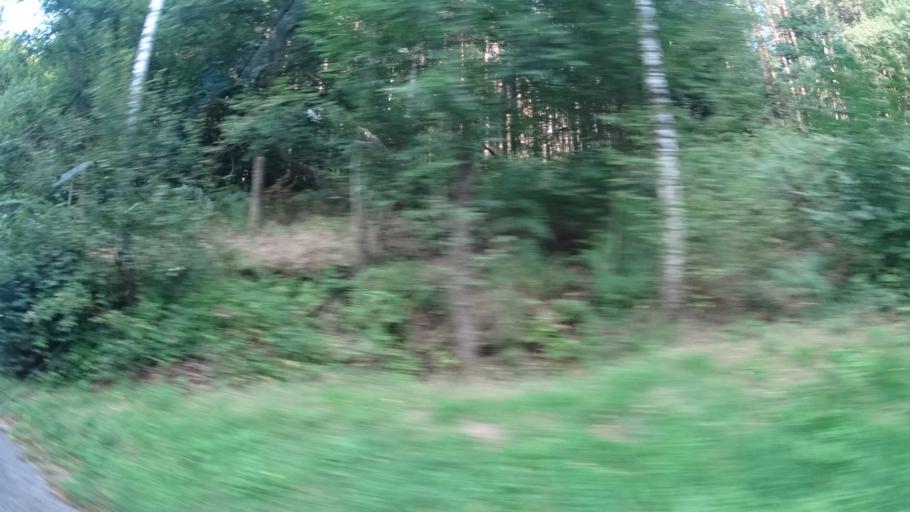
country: DE
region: Hesse
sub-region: Regierungsbezirk Darmstadt
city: Rothenberg
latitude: 49.5512
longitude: 8.9001
